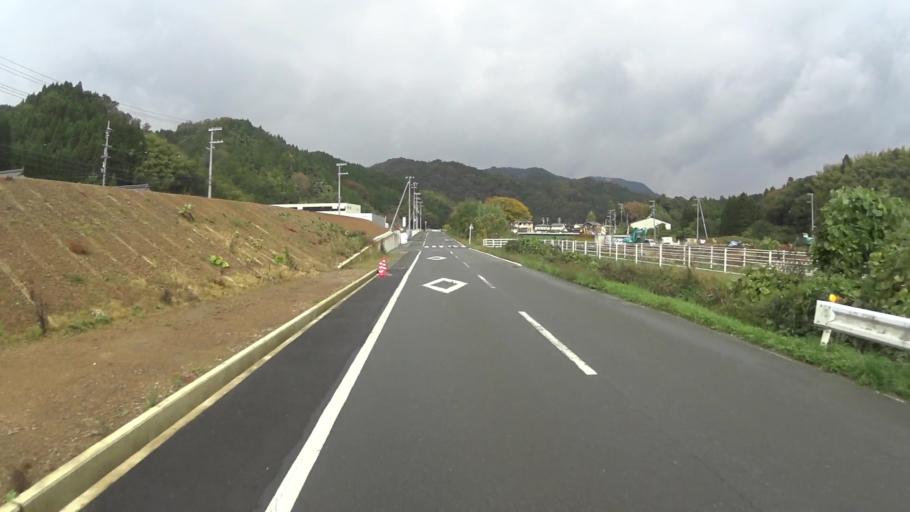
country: JP
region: Kyoto
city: Fukuchiyama
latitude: 35.3968
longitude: 135.1496
